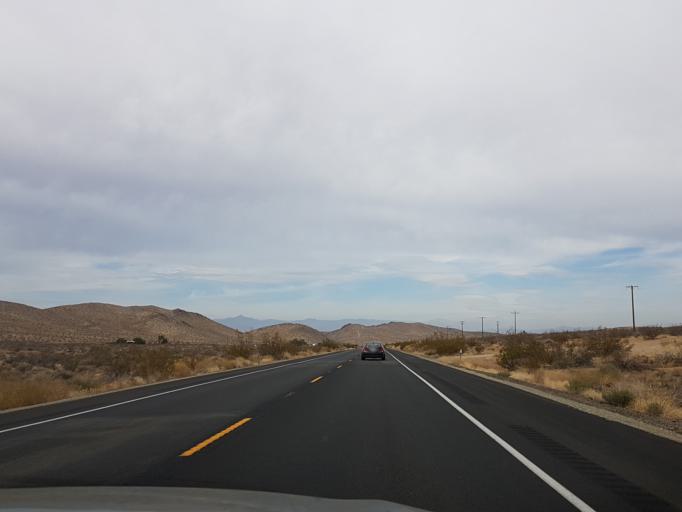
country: US
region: California
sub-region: Kern County
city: Ridgecrest
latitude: 35.5285
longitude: -117.6787
